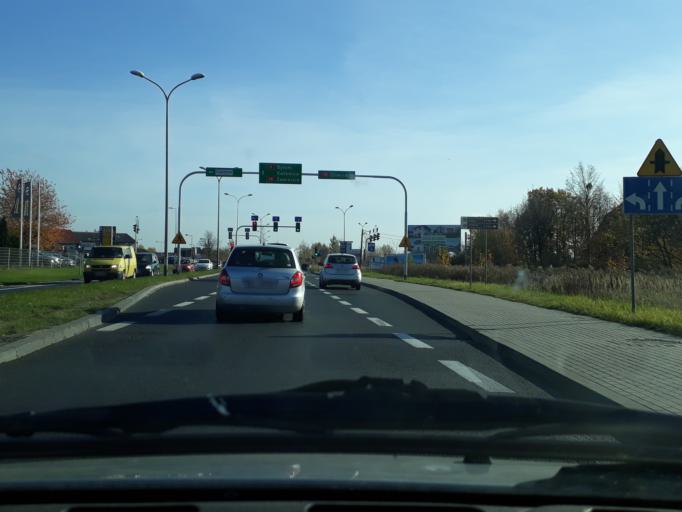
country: PL
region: Silesian Voivodeship
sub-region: Powiat tarnogorski
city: Tarnowskie Gory
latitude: 50.4366
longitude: 18.8446
